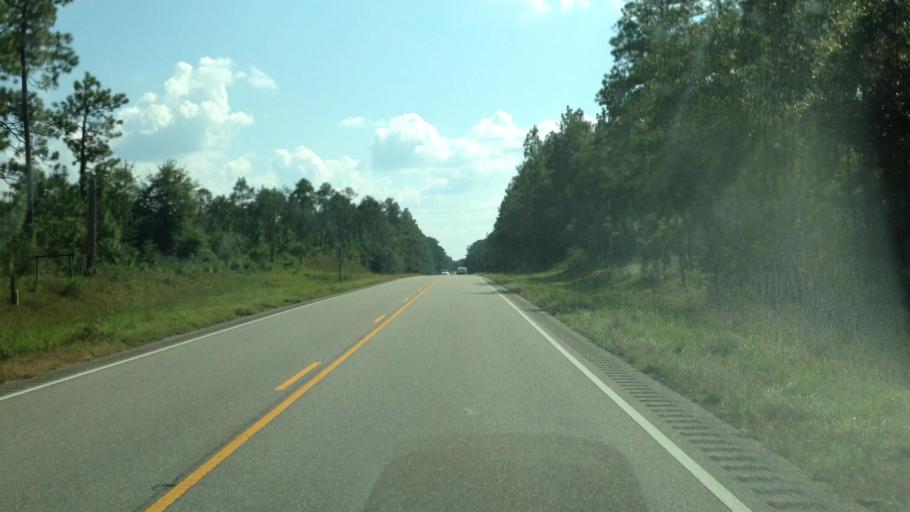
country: US
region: Florida
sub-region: Okaloosa County
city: Crestview
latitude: 31.0016
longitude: -86.6256
